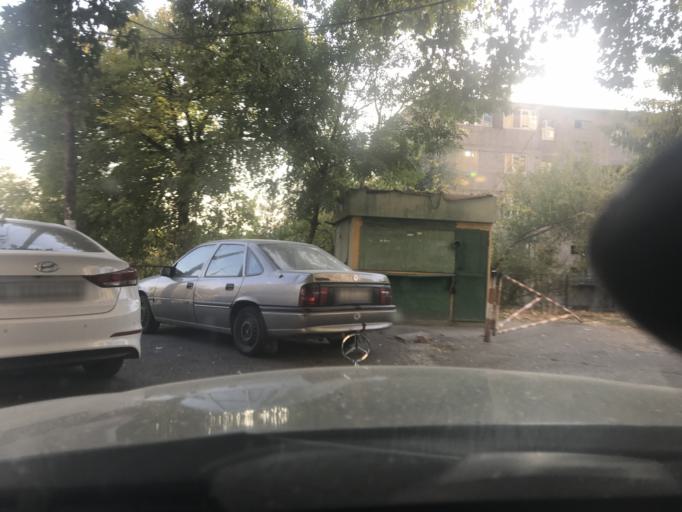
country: KZ
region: Ongtustik Qazaqstan
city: Shymkent
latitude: 42.3014
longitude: 69.6058
